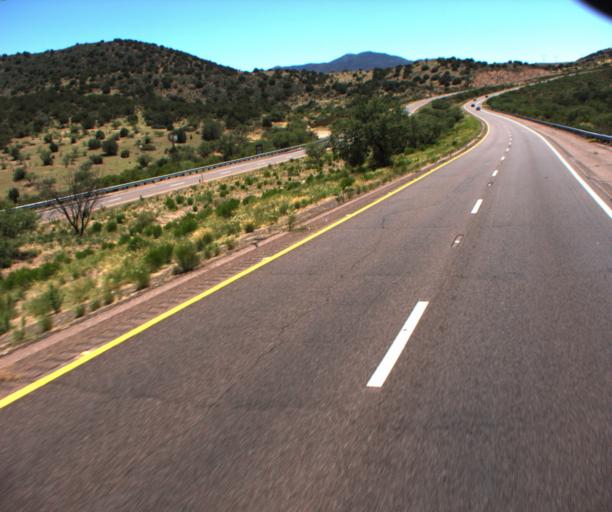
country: US
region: Arizona
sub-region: Gila County
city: Tonto Basin
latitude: 34.0032
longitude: -111.3578
